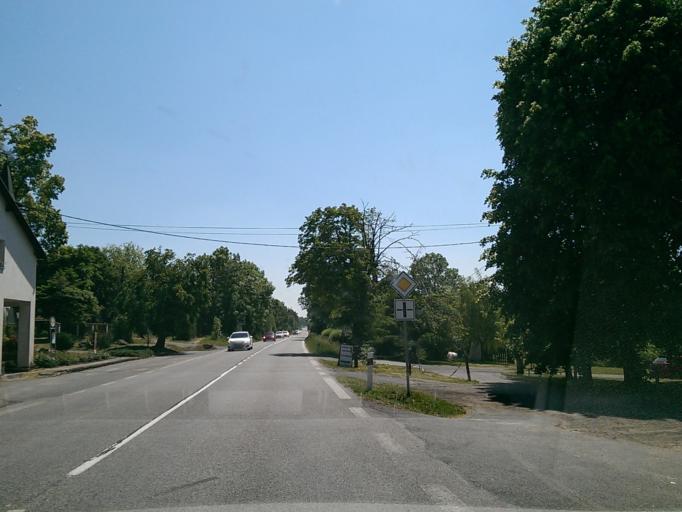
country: CZ
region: Liberecky
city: Rovensko pod Troskami
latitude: 50.5438
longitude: 15.2224
